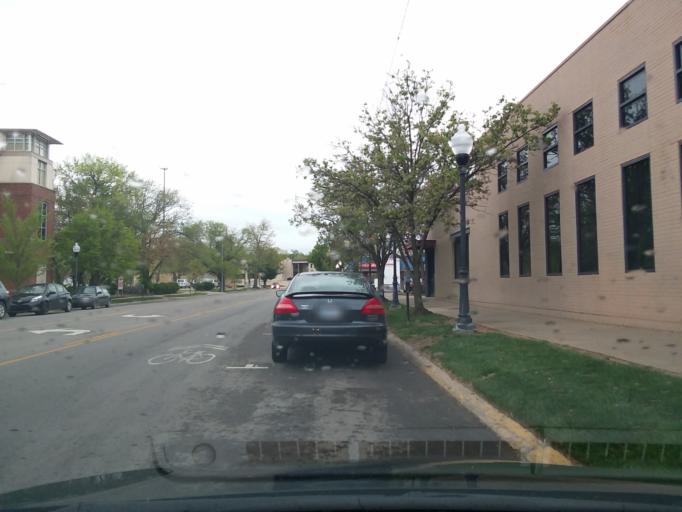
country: US
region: Kansas
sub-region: Douglas County
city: Lawrence
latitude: 38.9655
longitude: -95.2348
